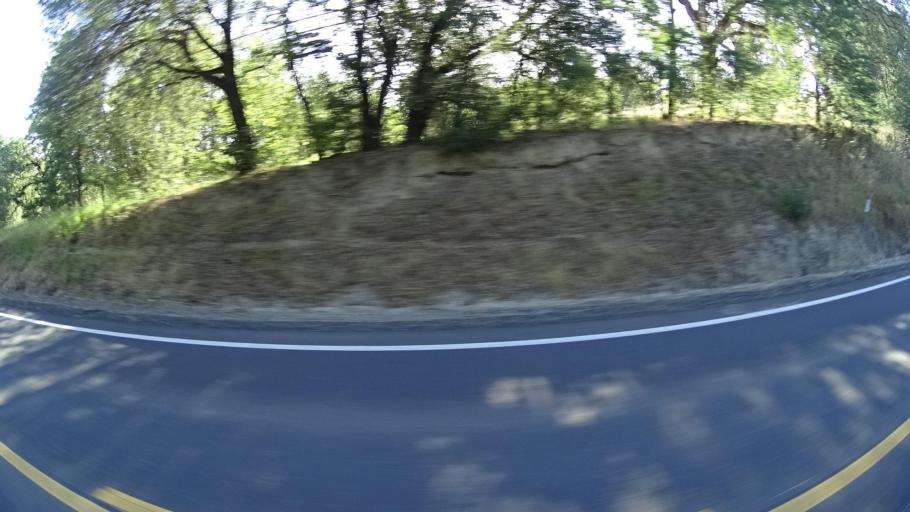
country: US
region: California
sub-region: Lake County
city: Upper Lake
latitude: 39.1505
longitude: -122.9201
